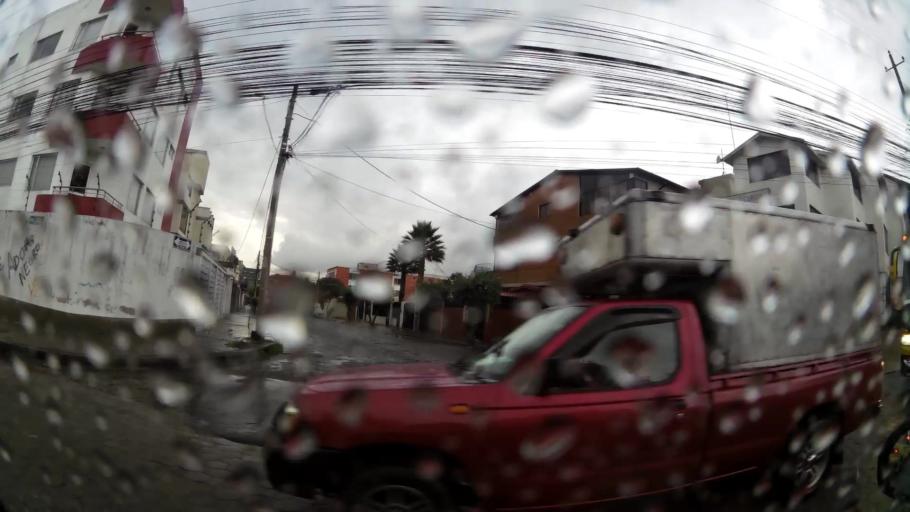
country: EC
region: Pichincha
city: Quito
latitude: -0.1597
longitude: -78.4645
